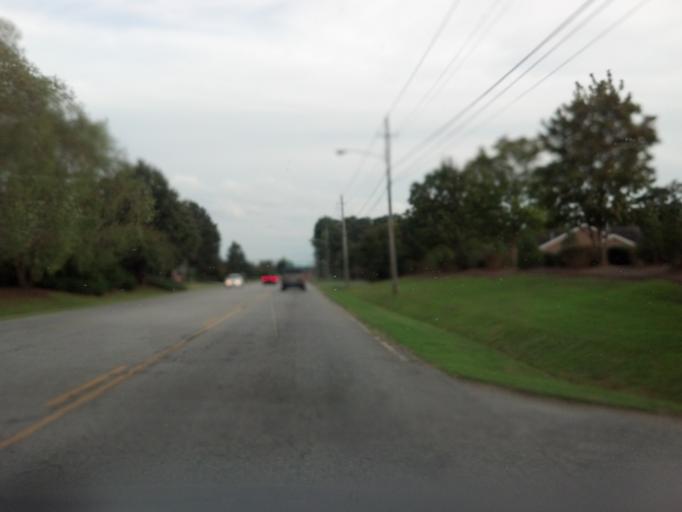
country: US
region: North Carolina
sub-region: Pitt County
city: Summerfield
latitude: 35.5586
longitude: -77.3863
